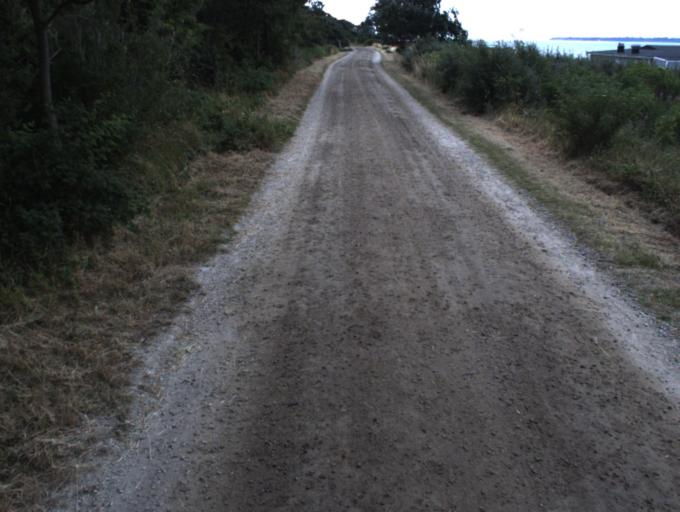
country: SE
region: Skane
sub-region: Helsingborg
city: Rydeback
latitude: 55.9644
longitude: 12.7585
